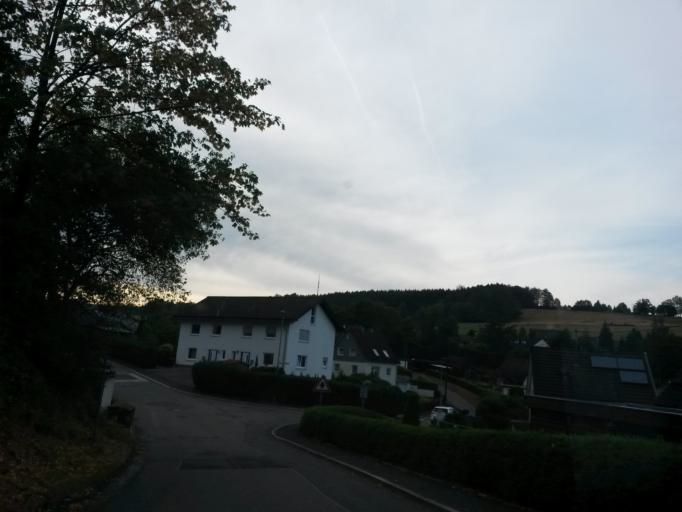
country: DE
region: North Rhine-Westphalia
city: Bergneustadt
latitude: 51.0480
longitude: 7.6185
